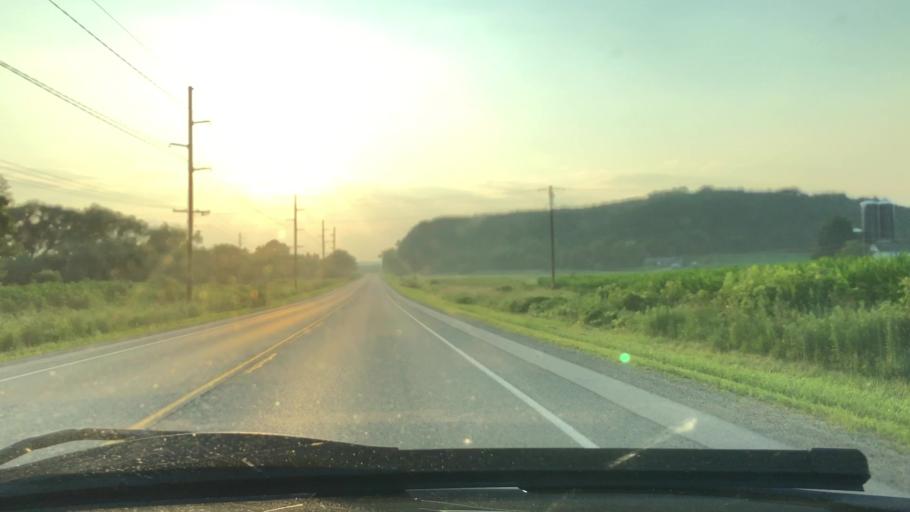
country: US
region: Wisconsin
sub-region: Dane County
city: Black Earth
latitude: 43.1322
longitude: -89.7250
